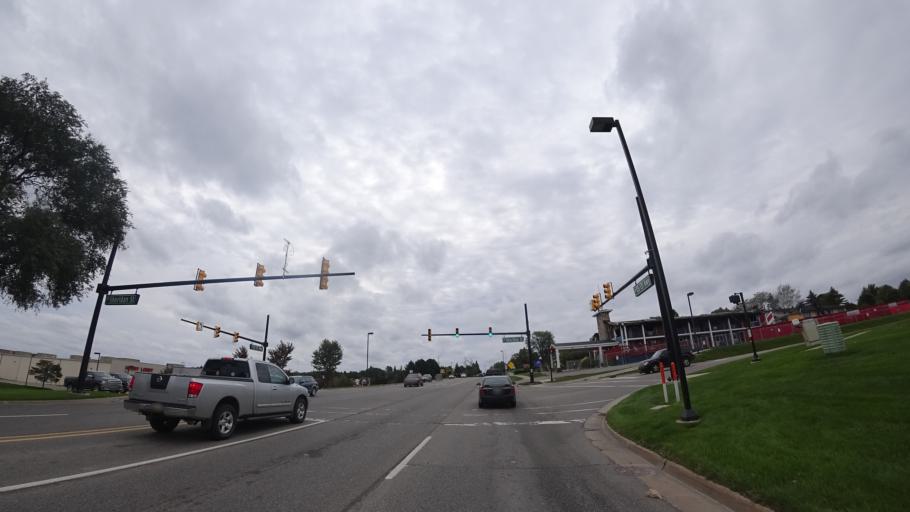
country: US
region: Michigan
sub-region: Emmet County
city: Petoskey
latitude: 45.3633
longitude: -84.9710
